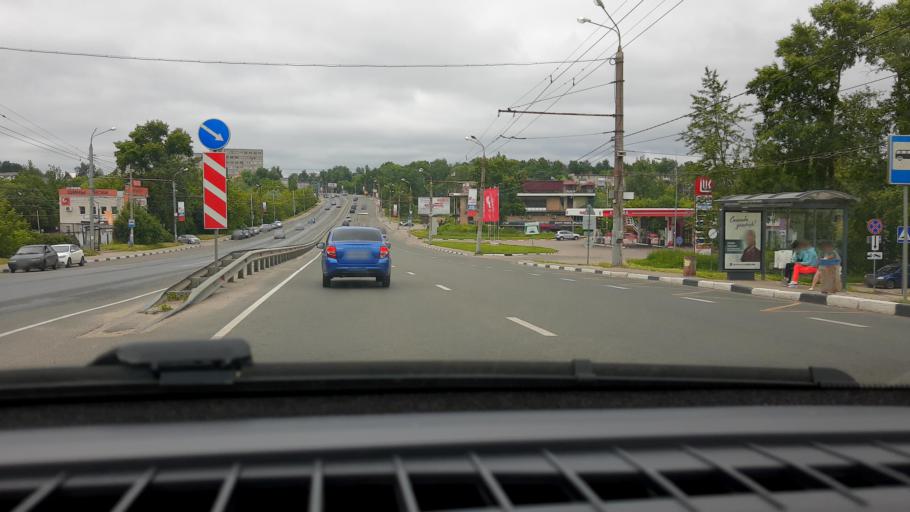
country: RU
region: Nizjnij Novgorod
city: Nizhniy Novgorod
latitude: 56.2869
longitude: 44.0356
